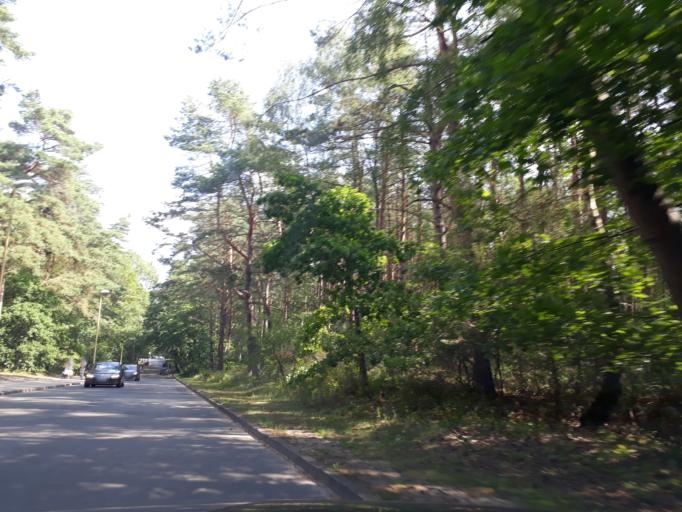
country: PL
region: West Pomeranian Voivodeship
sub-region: Swinoujscie
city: Swinoujscie
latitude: 53.9233
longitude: 14.2268
